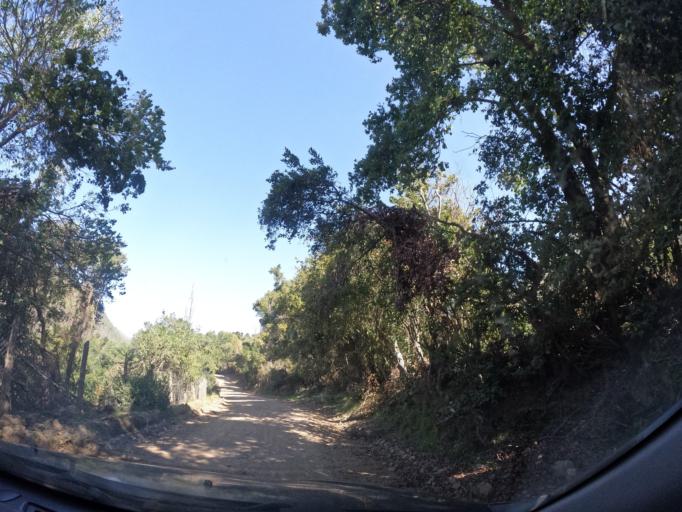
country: CL
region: Maule
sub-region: Provincia de Linares
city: Longavi
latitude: -36.2807
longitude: -71.4168
